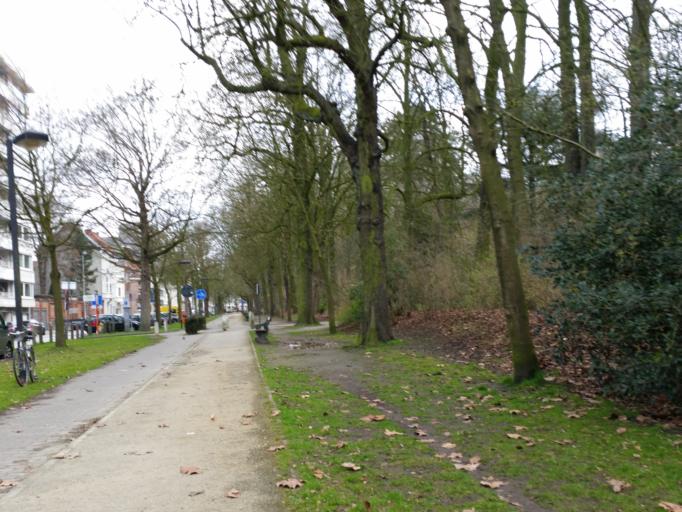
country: BE
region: Flanders
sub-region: Provincie Oost-Vlaanderen
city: Gent
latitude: 51.0382
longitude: 3.7177
